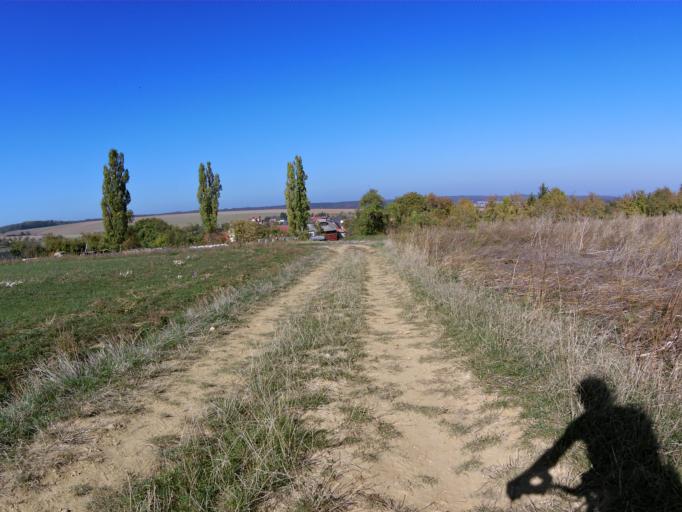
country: DE
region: Bavaria
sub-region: Regierungsbezirk Unterfranken
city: Geroldshausen
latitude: 49.7004
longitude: 9.9087
